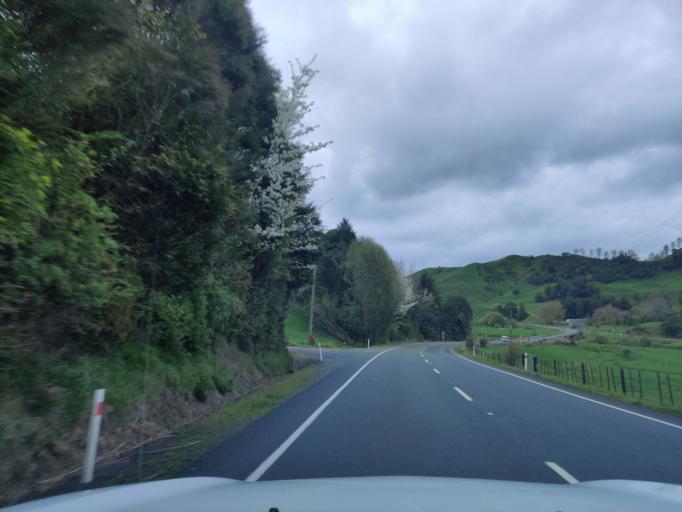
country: NZ
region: Waikato
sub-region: Otorohanga District
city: Otorohanga
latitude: -38.4910
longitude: 175.1879
